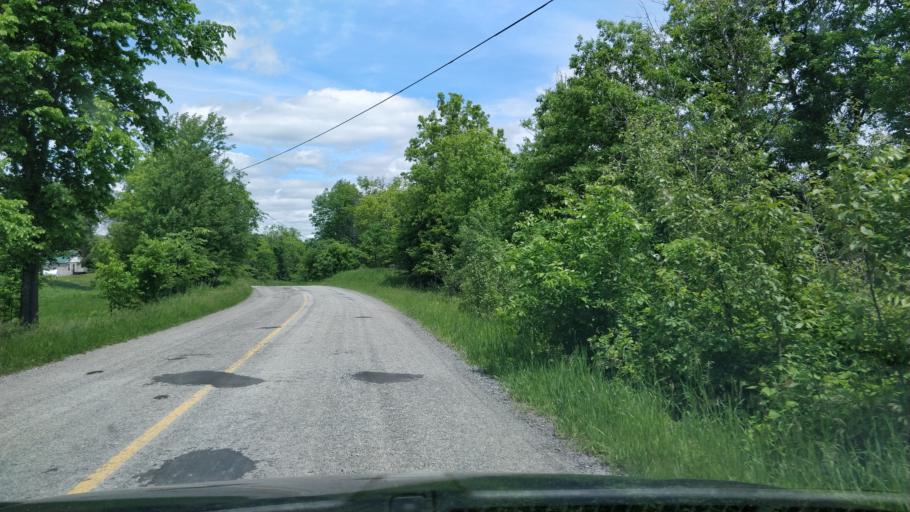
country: CA
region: Ontario
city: Perth
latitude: 44.7356
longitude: -76.5034
